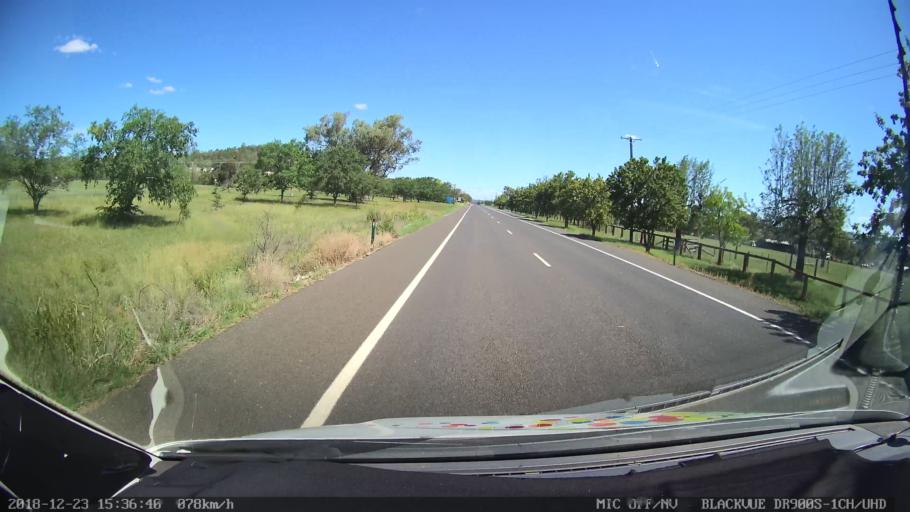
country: AU
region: New South Wales
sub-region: Tamworth Municipality
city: Tamworth
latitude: -31.0437
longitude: 150.8875
